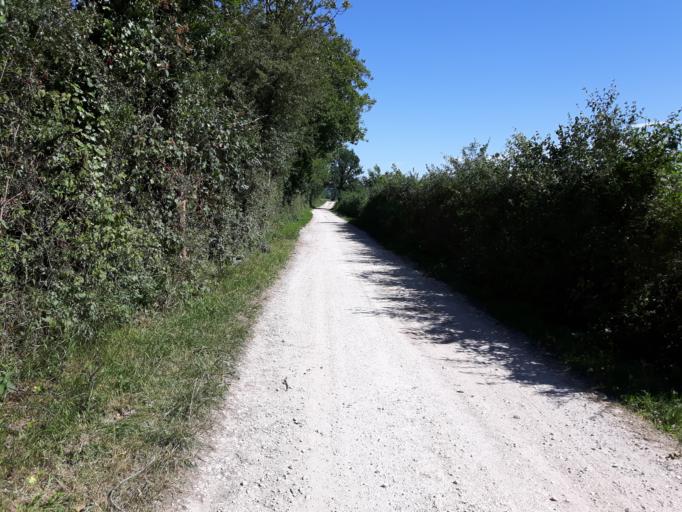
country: FR
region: Franche-Comte
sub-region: Departement du Jura
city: Mouchard
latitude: 47.0174
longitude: 5.8505
